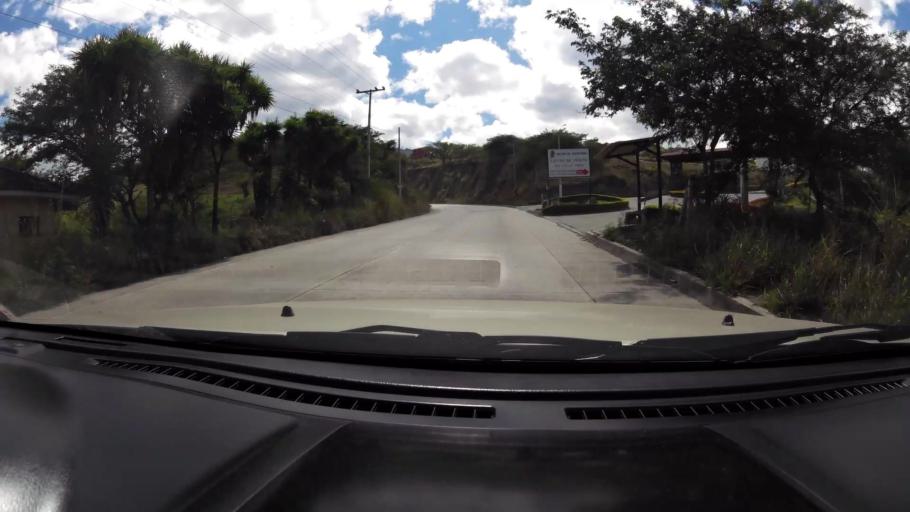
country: EC
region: Azuay
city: Cuenca
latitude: -3.2195
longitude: -79.1998
